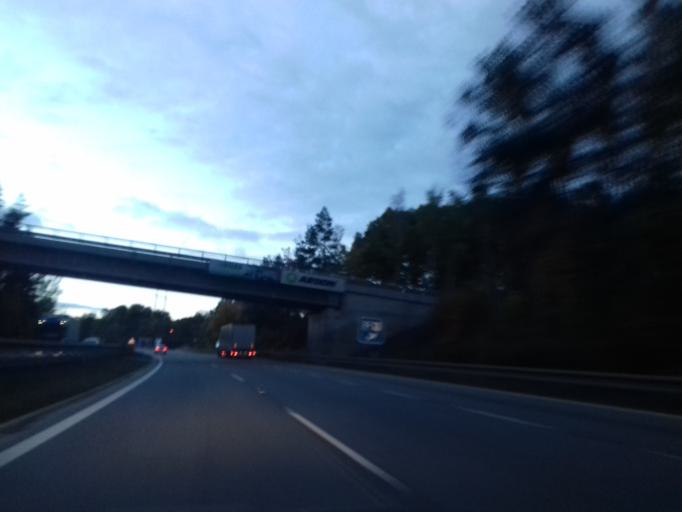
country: CZ
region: Central Bohemia
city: Divisov
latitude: 49.7943
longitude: 14.9236
